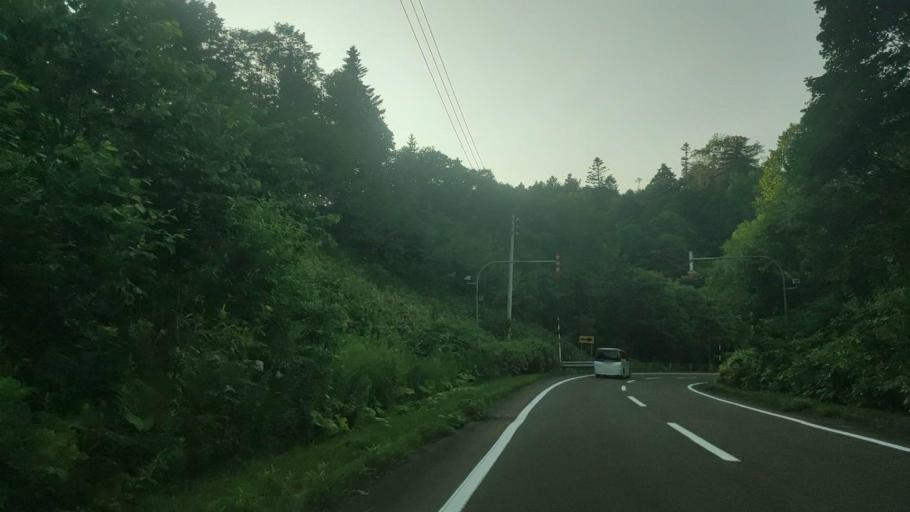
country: JP
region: Hokkaido
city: Bibai
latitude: 43.1686
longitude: 142.0725
